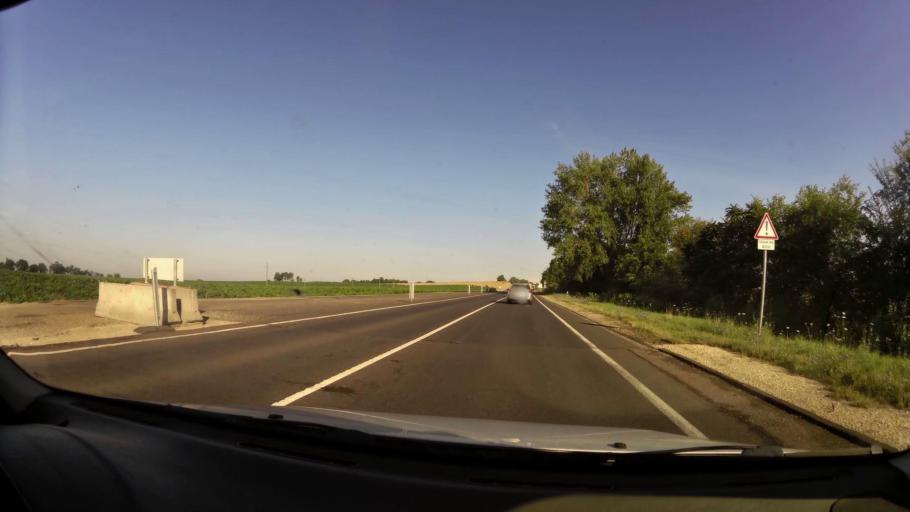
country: HU
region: Pest
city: Cegledbercel
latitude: 47.2202
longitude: 19.7008
